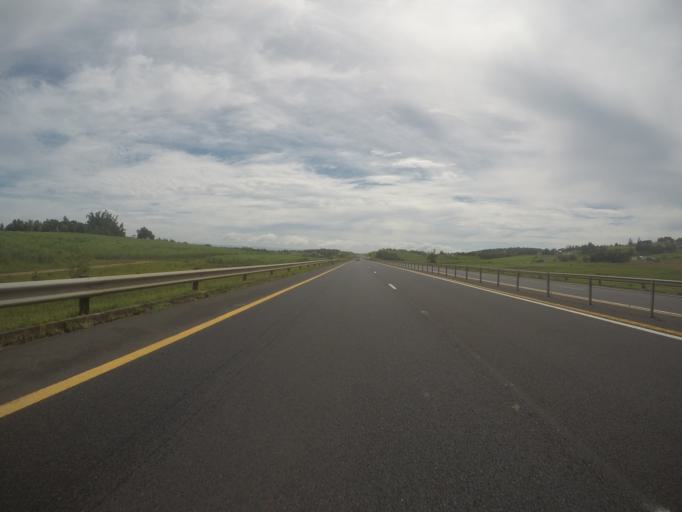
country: ZA
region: KwaZulu-Natal
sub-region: iLembe District Municipality
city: Mandeni
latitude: -29.0694
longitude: 31.6205
